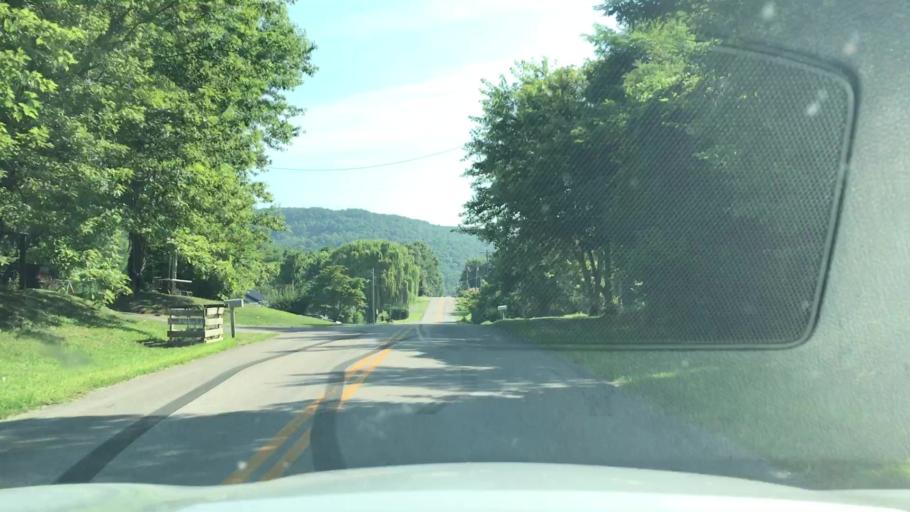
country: US
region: Kentucky
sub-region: Clinton County
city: Albany
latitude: 36.7017
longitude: -85.0390
